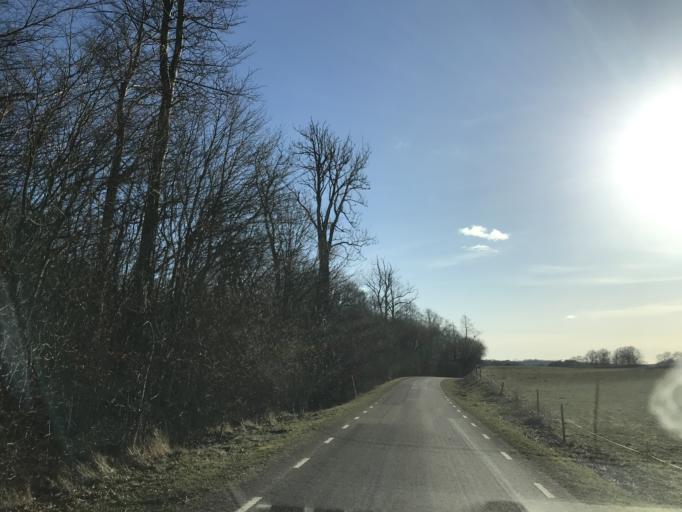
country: SE
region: Skane
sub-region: Ystads Kommun
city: Ystad
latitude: 55.5503
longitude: 13.8064
